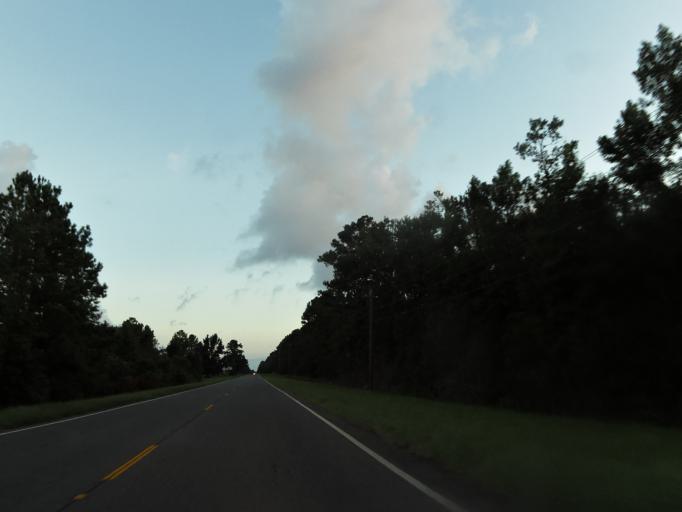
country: US
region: Georgia
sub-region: Camden County
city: Kingsland
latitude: 30.7727
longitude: -81.6869
